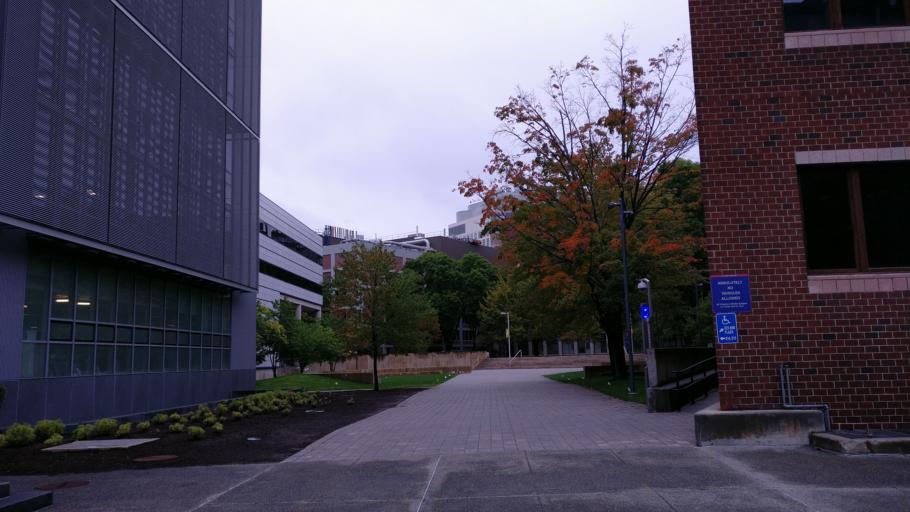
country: US
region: Massachusetts
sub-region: Middlesex County
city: Cambridge
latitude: 42.3605
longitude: -71.0869
